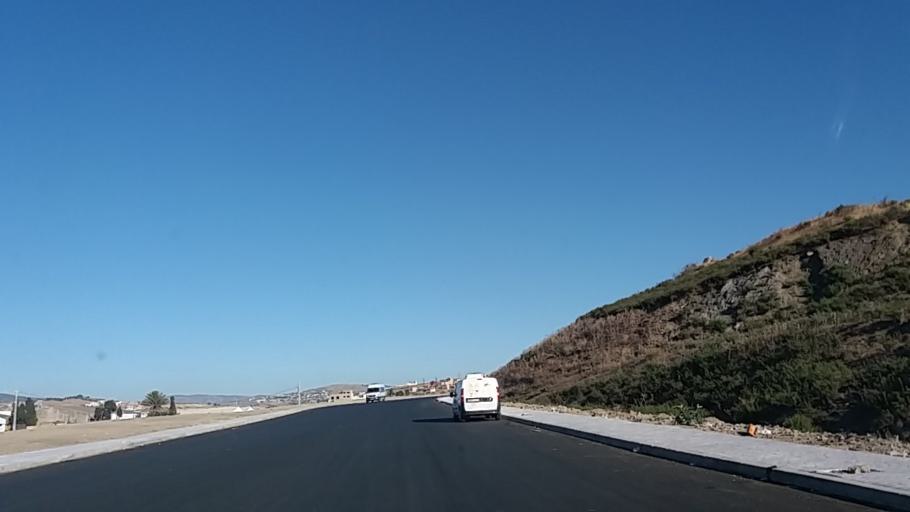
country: MA
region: Tanger-Tetouan
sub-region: Tanger-Assilah
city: Tangier
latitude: 35.7393
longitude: -5.7838
